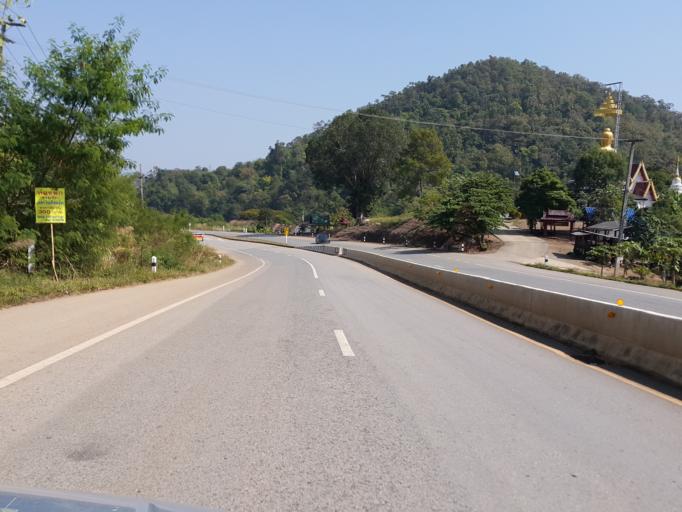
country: TH
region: Lampang
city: Wang Nuea
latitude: 19.1127
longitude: 99.4587
